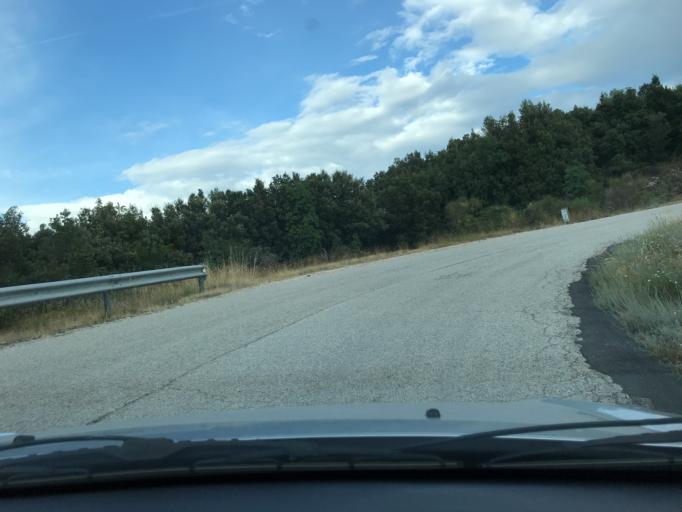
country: IT
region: Umbria
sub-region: Provincia di Terni
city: Montecchio
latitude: 42.6912
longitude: 12.2951
